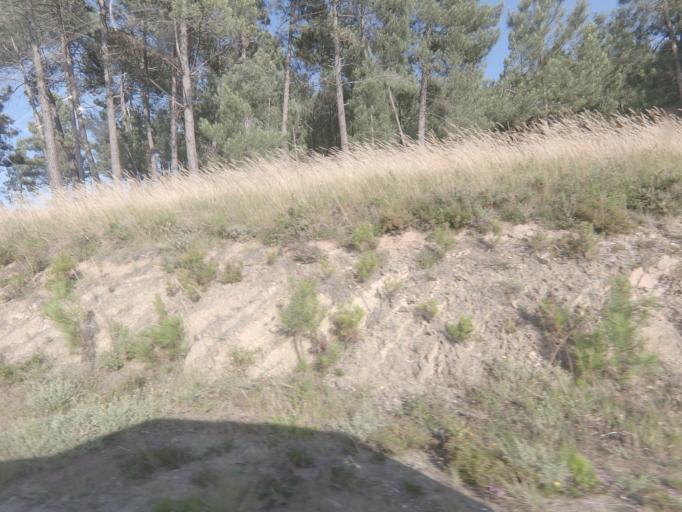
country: PT
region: Vila Real
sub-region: Sabrosa
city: Vilela
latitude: 41.2362
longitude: -7.6031
